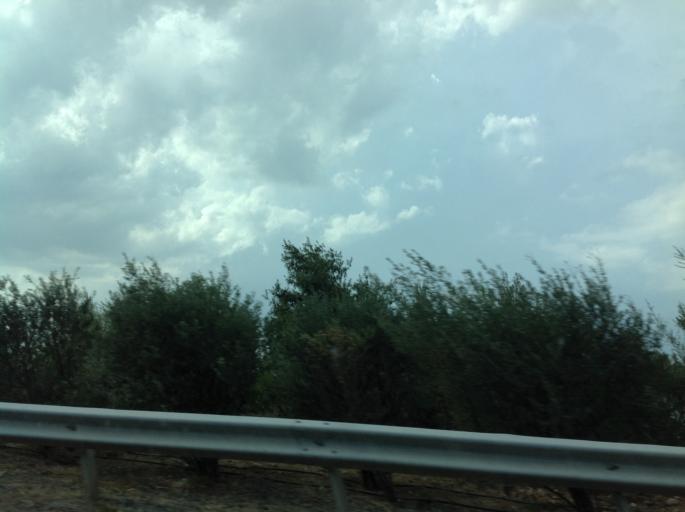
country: GR
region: Attica
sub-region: Nomarchia Athinas
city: Cholargos
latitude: 37.9919
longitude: 23.8167
